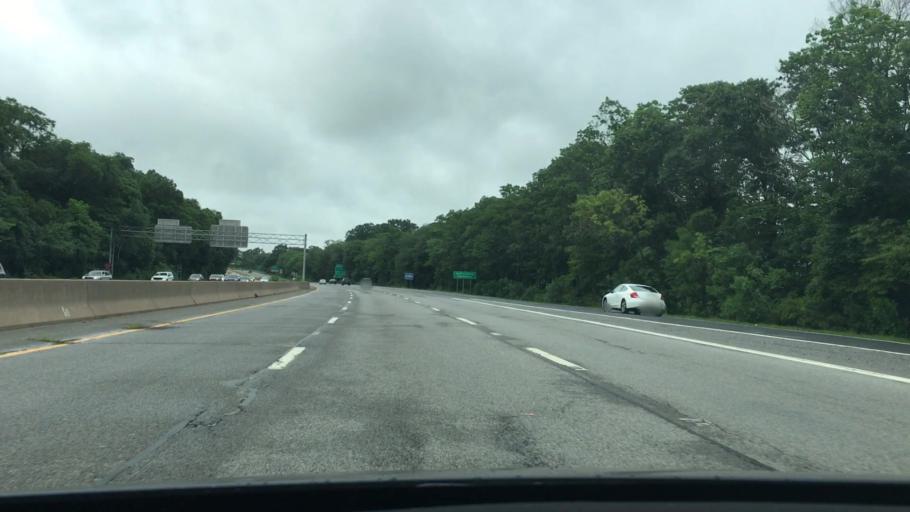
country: US
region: New York
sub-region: Nassau County
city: Syosset
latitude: 40.8095
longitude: -73.4917
